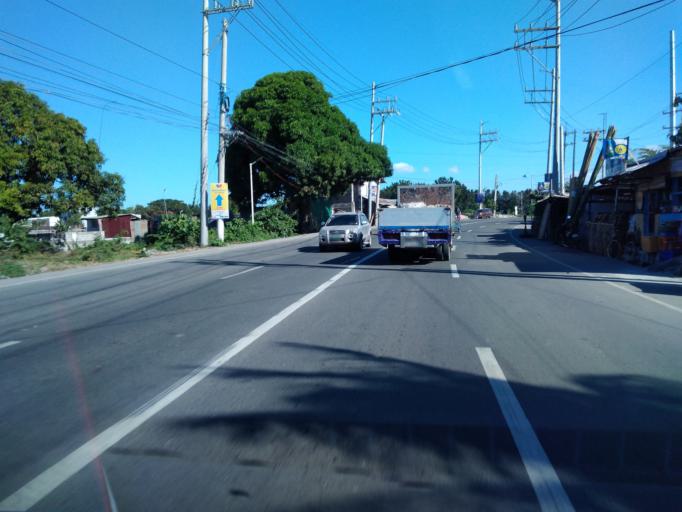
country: PH
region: Central Luzon
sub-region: Province of Bulacan
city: Santa Maria
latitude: 14.8163
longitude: 120.9487
